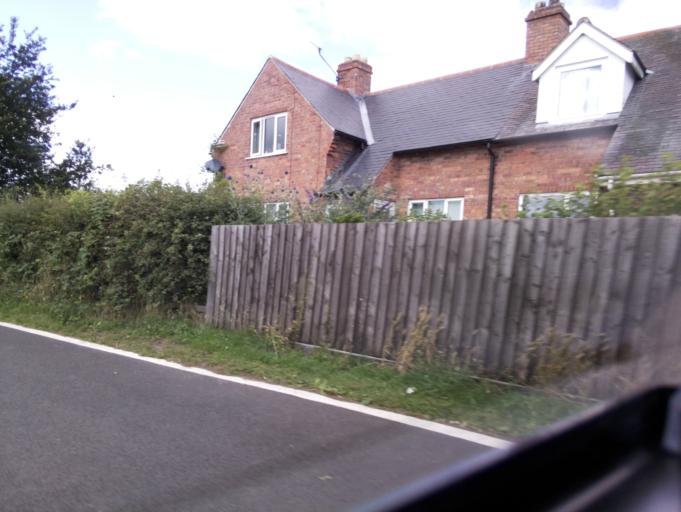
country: GB
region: England
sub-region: Nottinghamshire
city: West Bridgford
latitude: 52.9281
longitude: -1.0963
